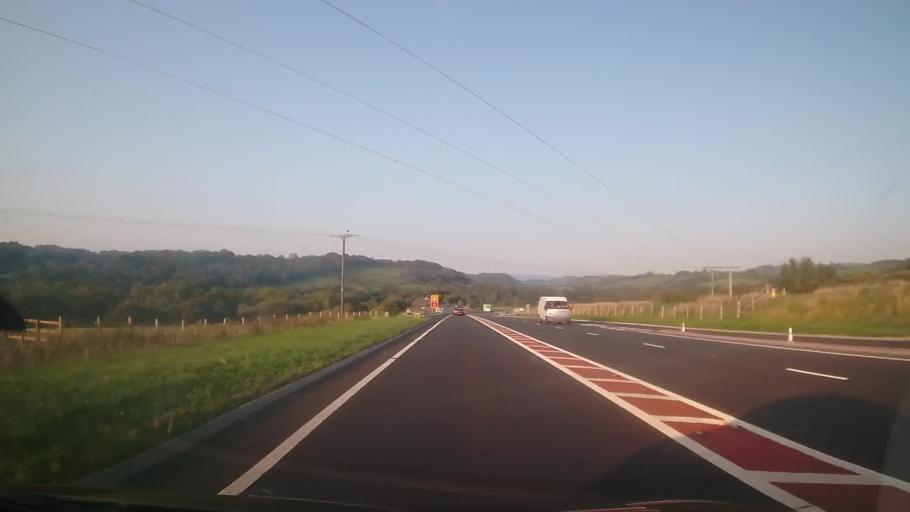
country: GB
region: Wales
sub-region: Sir Powys
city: Newtown
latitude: 52.5179
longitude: -3.2865
